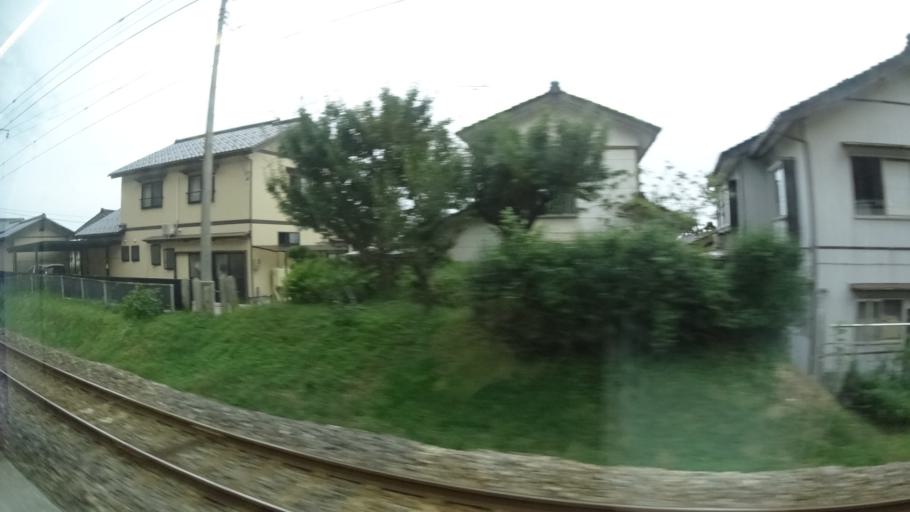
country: JP
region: Yamagata
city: Tsuruoka
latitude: 38.6285
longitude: 139.5906
